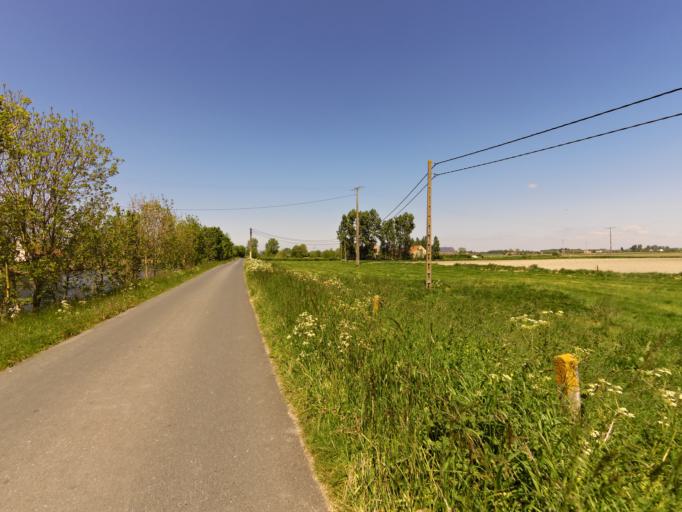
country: BE
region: Flanders
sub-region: Provincie West-Vlaanderen
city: Diksmuide
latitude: 51.0557
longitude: 2.8486
